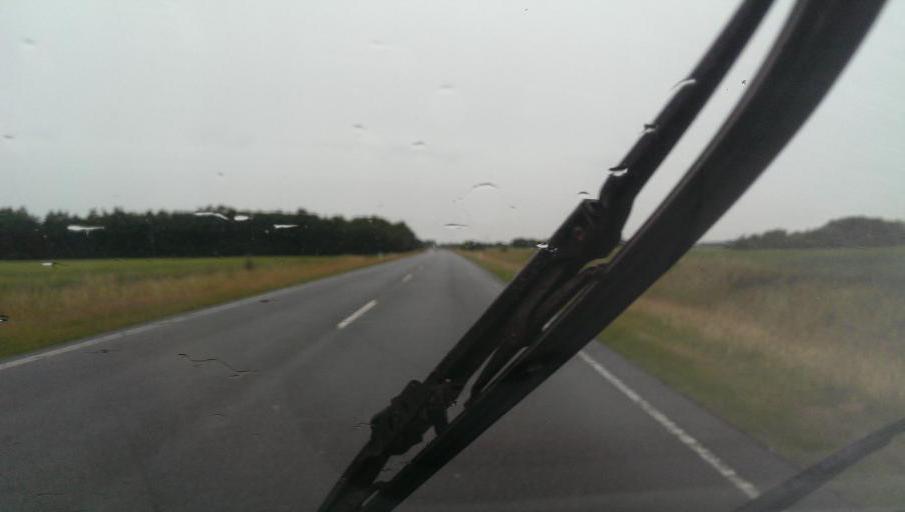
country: DK
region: South Denmark
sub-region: Esbjerg Kommune
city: Esbjerg
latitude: 55.5319
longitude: 8.4281
